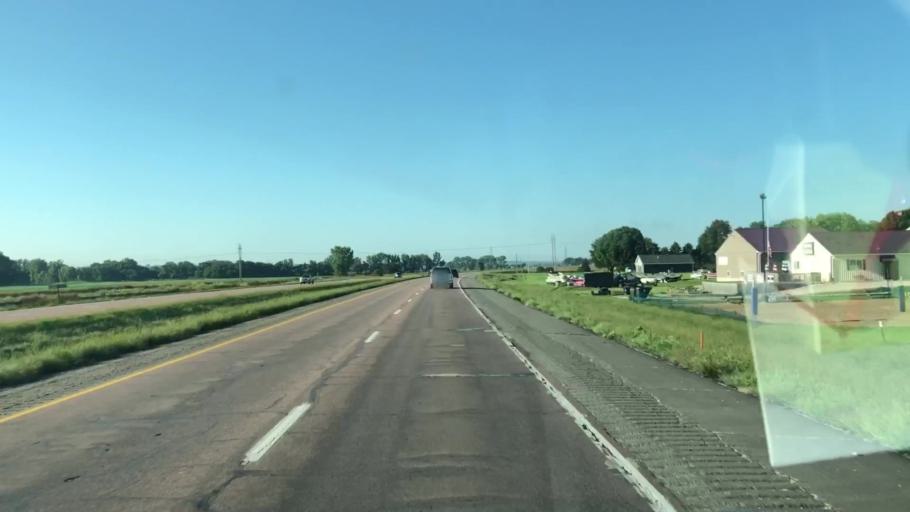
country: US
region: Iowa
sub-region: Woodbury County
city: Sioux City
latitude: 42.6154
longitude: -96.2954
